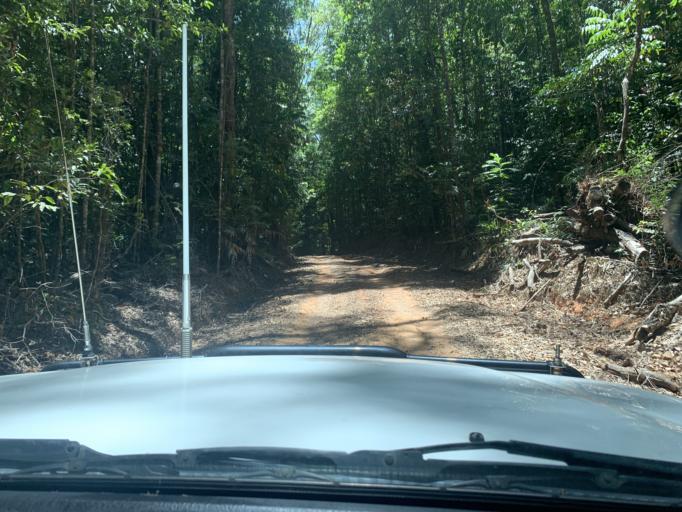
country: AU
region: Queensland
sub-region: Cairns
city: Redlynch
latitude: -16.9413
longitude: 145.6275
